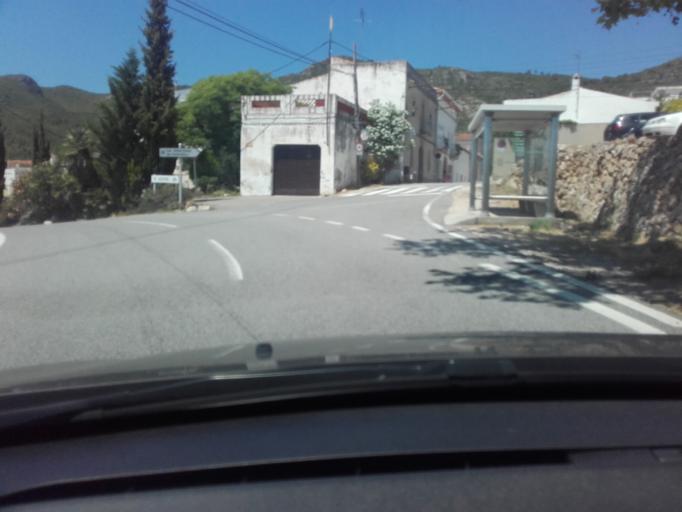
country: ES
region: Catalonia
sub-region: Provincia de Tarragona
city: la Bisbal del Penedes
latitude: 41.3144
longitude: 1.4533
